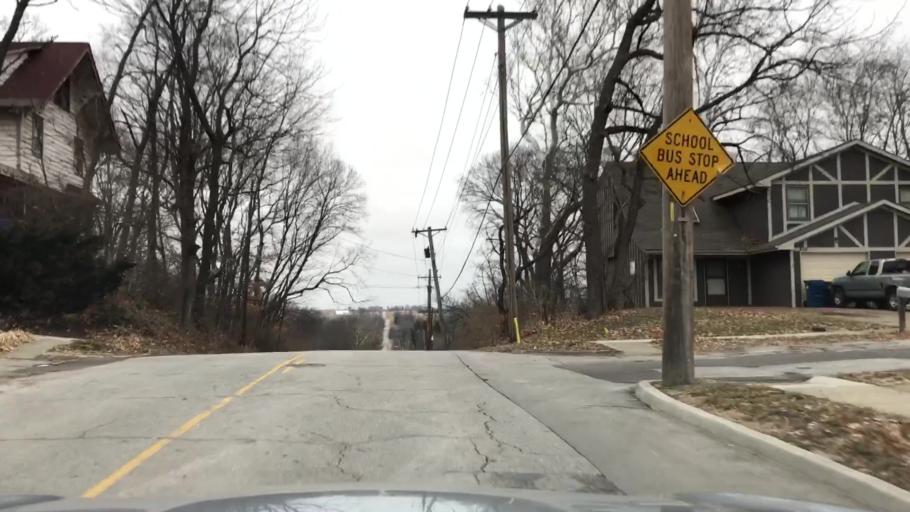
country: US
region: Missouri
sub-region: Clay County
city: Liberty
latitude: 39.2519
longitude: -94.4166
